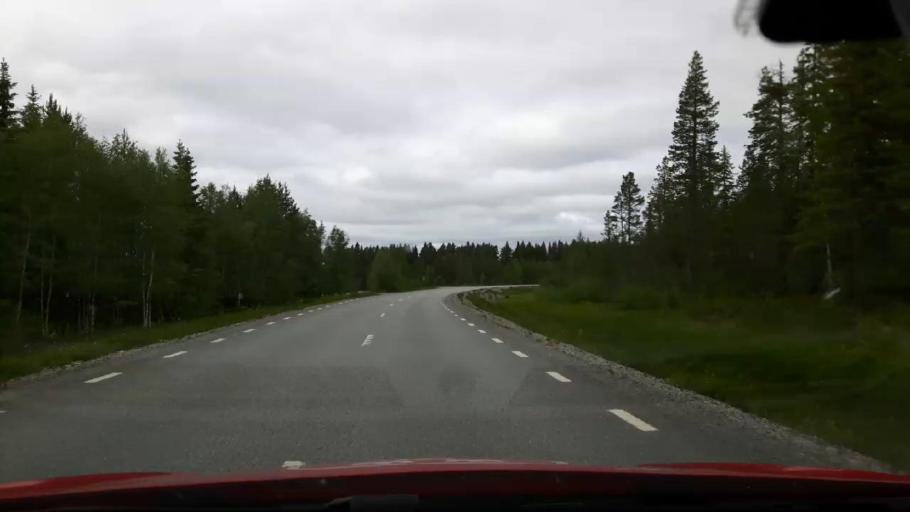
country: SE
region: Jaemtland
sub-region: OEstersunds Kommun
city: Lit
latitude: 63.6827
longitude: 14.6746
